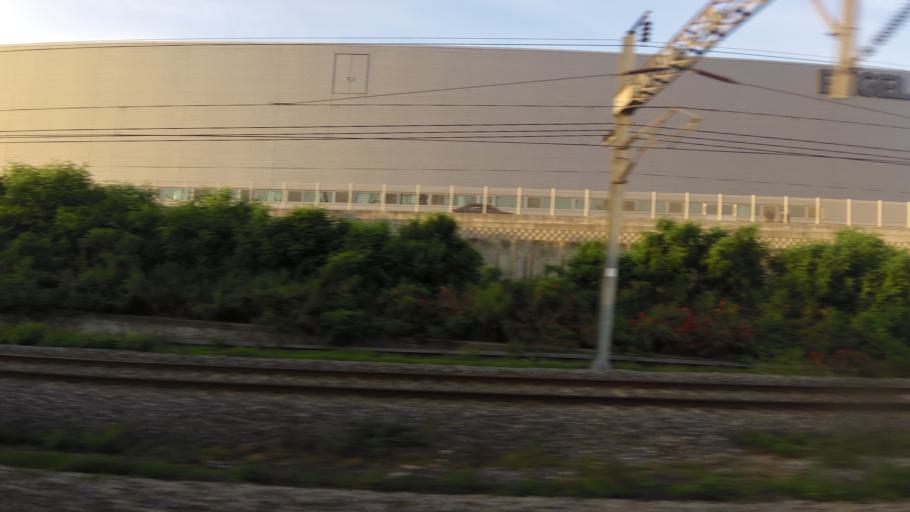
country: KR
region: Gyeonggi-do
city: Osan
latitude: 37.0412
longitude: 127.0626
